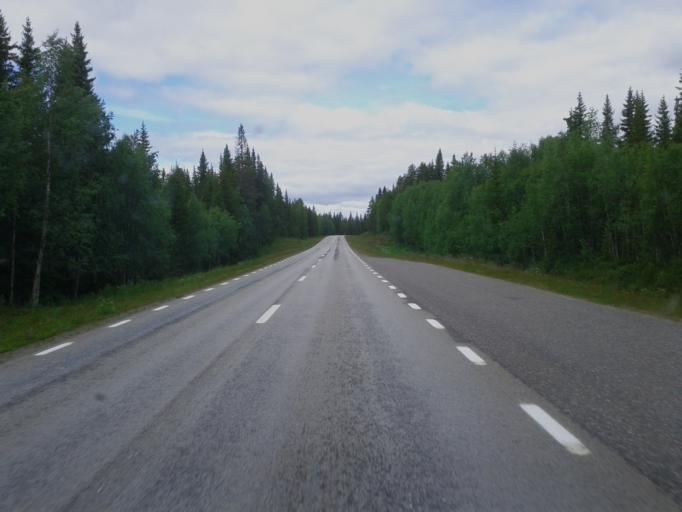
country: SE
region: Vaesterbotten
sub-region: Storumans Kommun
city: Fristad
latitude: 65.3648
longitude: 16.5265
